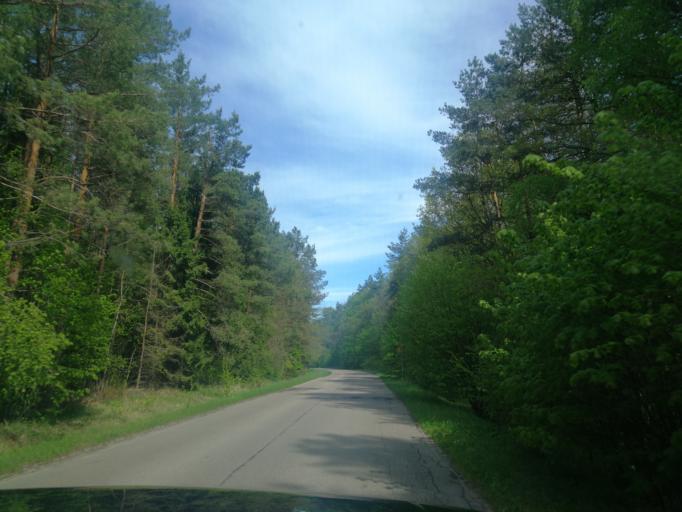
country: PL
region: Warmian-Masurian Voivodeship
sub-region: Powiat ilawski
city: Ilawa
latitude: 53.6896
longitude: 19.6912
